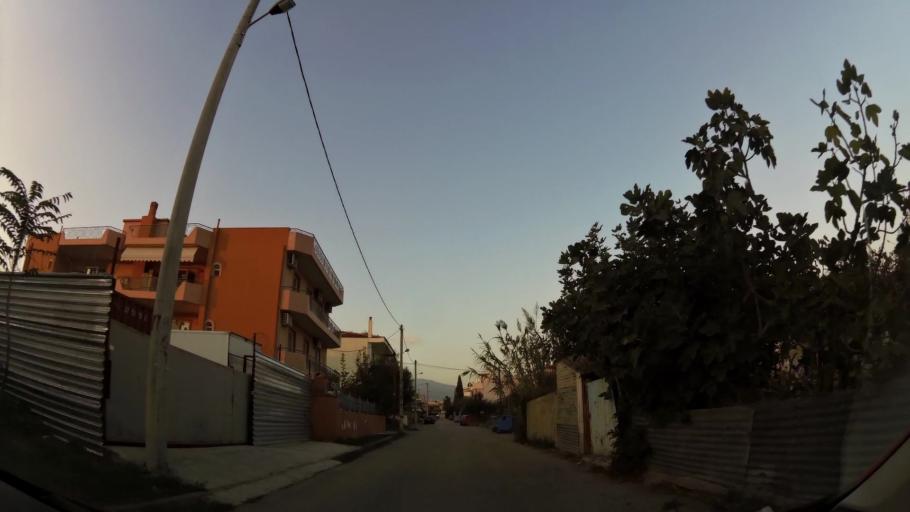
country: GR
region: Attica
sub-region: Nomarchia Anatolikis Attikis
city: Acharnes
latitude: 38.0916
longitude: 23.7489
